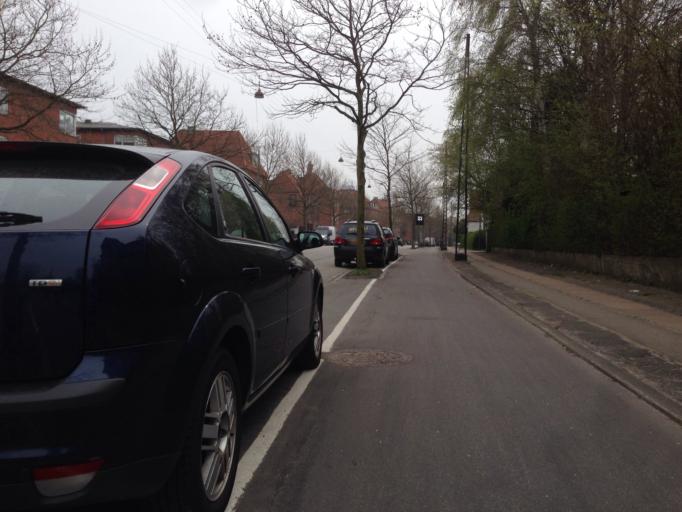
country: DK
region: Capital Region
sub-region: Frederiksberg Kommune
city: Frederiksberg
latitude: 55.7260
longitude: 12.5262
